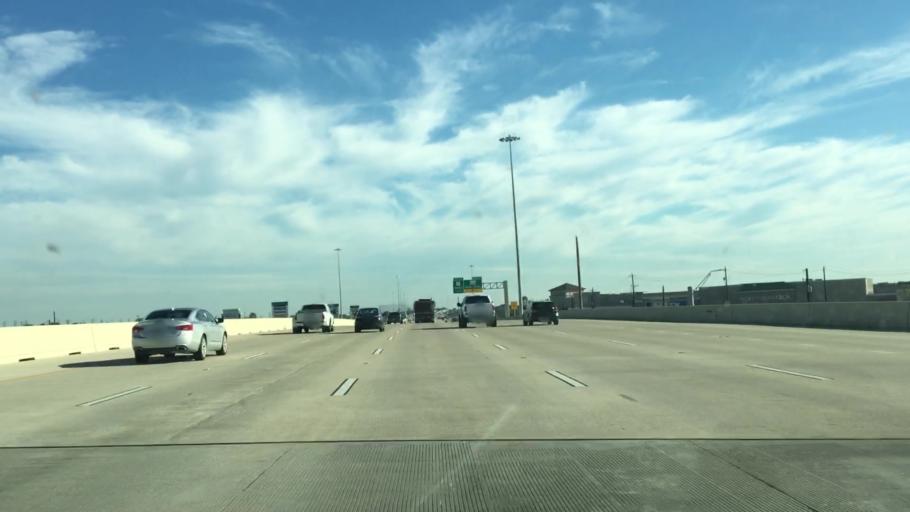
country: US
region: Texas
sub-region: Harris County
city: Webster
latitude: 29.5407
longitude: -95.1420
